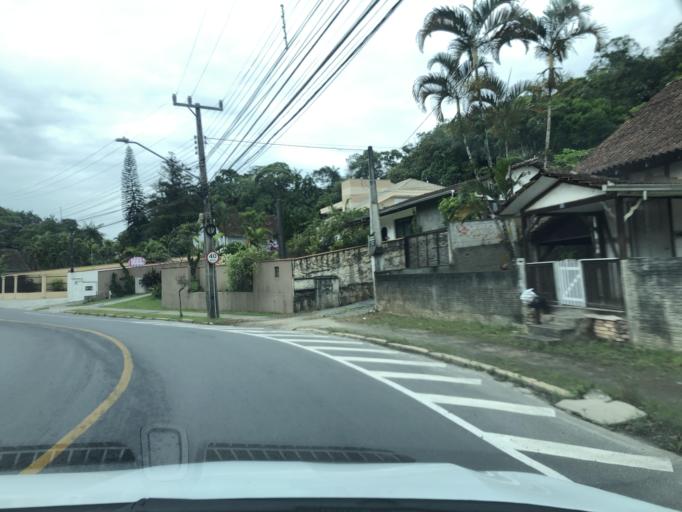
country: BR
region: Santa Catarina
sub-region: Joinville
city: Joinville
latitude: -26.3226
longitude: -48.8585
